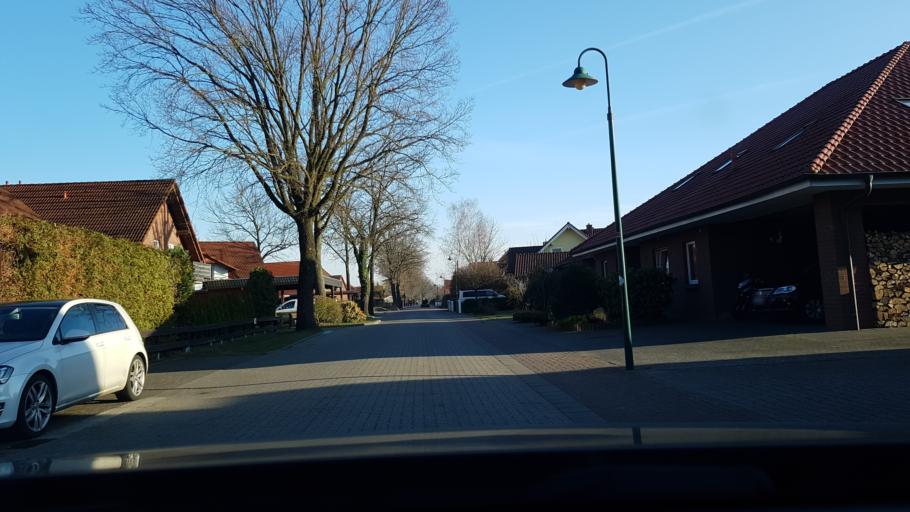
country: DE
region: Lower Saxony
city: Gifhorn
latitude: 52.5059
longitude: 10.5794
